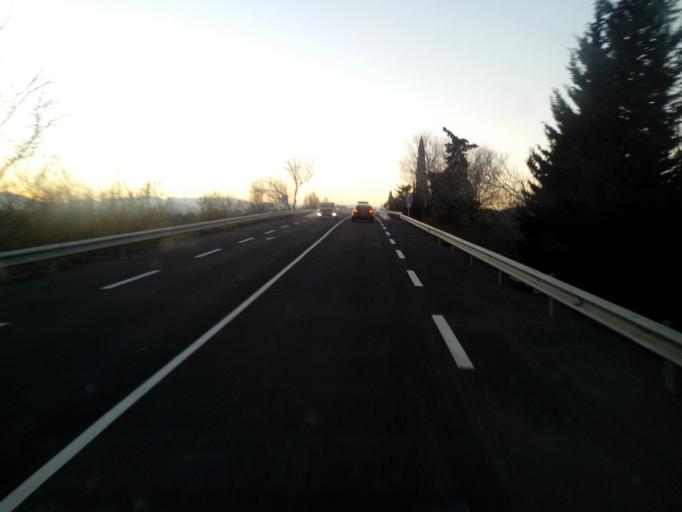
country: FR
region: Languedoc-Roussillon
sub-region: Departement des Pyrenees-Orientales
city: Rivesaltes
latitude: 42.7713
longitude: 2.8946
